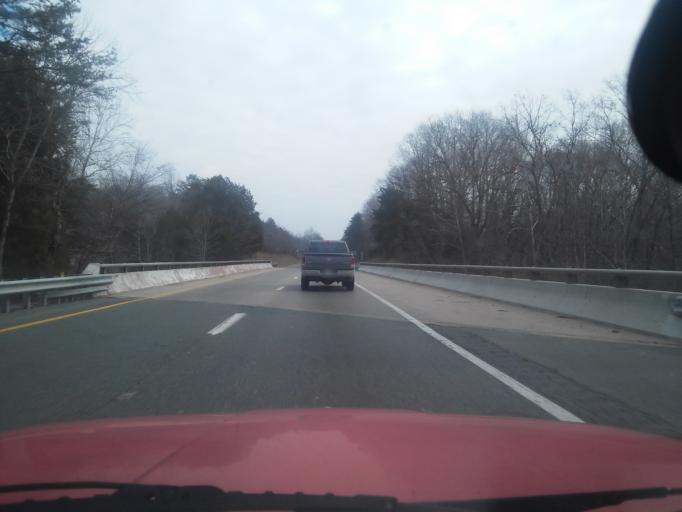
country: US
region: Virginia
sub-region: Fluvanna County
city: Lake Monticello
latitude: 37.9968
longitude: -78.2995
